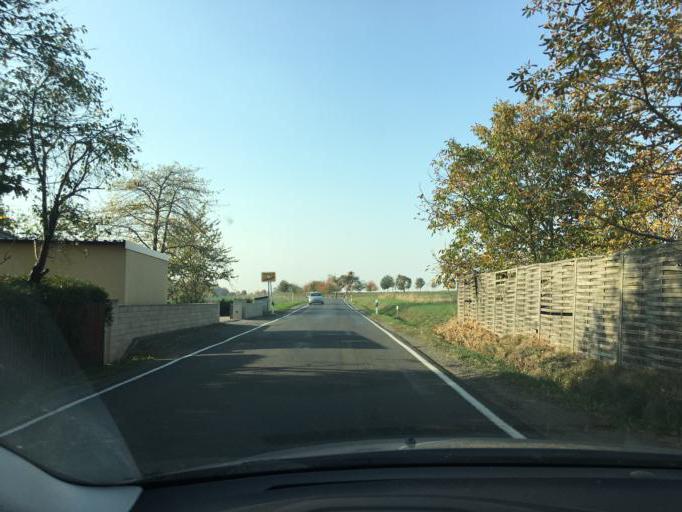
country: DE
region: Saxony
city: Mutzschen
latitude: 51.3192
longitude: 12.8535
